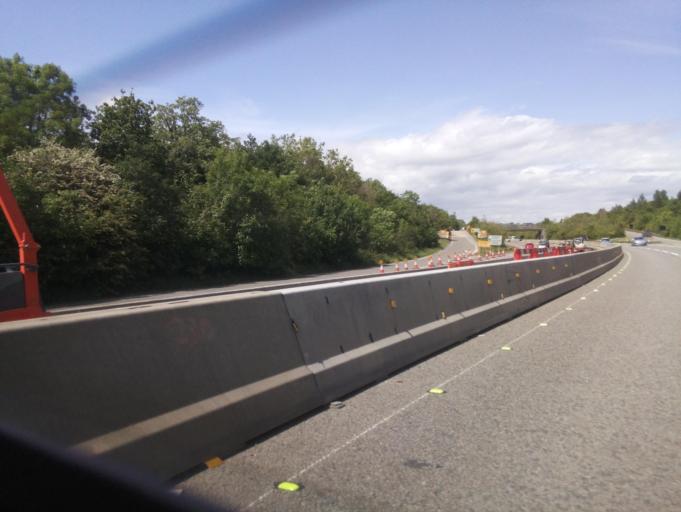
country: GB
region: England
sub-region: Devon
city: Chudleigh
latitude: 50.5927
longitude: -3.6126
